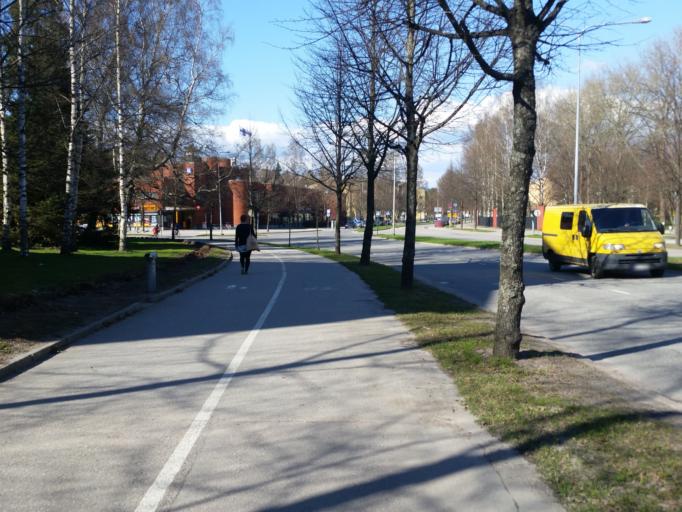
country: FI
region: Uusimaa
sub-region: Helsinki
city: Helsinki
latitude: 60.2149
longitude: 24.9585
